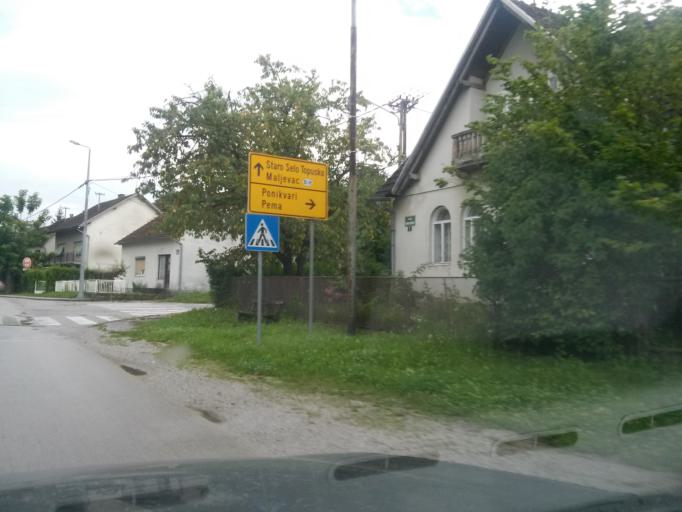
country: HR
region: Sisacko-Moslavacka
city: Gvozd
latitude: 45.2929
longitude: 15.9673
